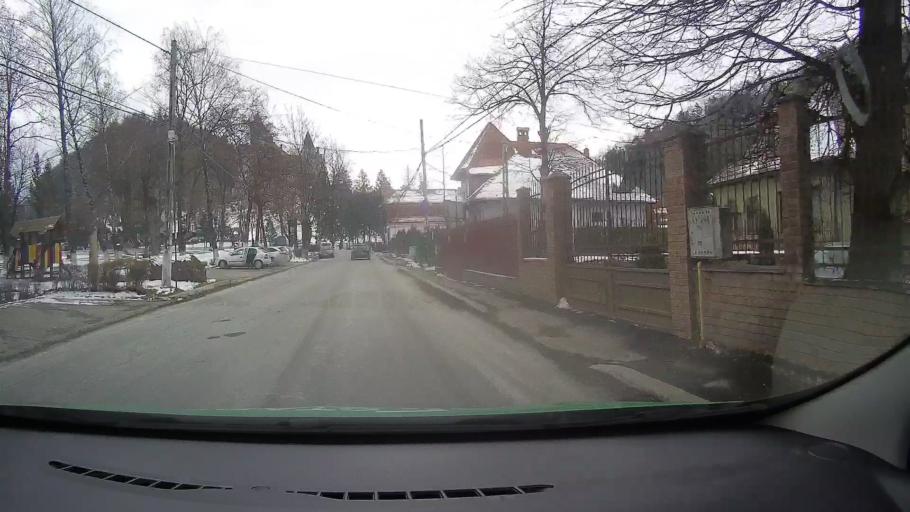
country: RO
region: Brasov
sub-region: Comuna Bran
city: Bran
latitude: 45.5170
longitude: 25.3667
